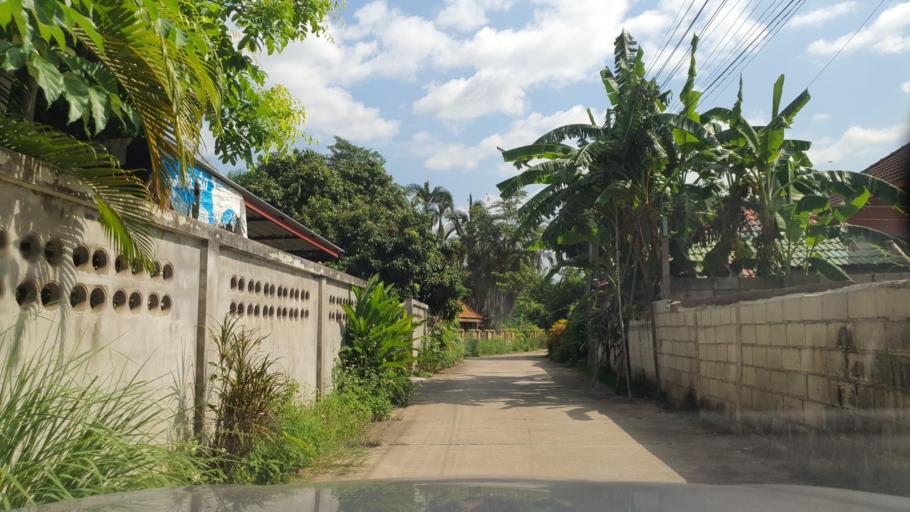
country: TH
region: Chiang Mai
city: Hang Dong
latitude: 18.7228
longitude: 98.9120
